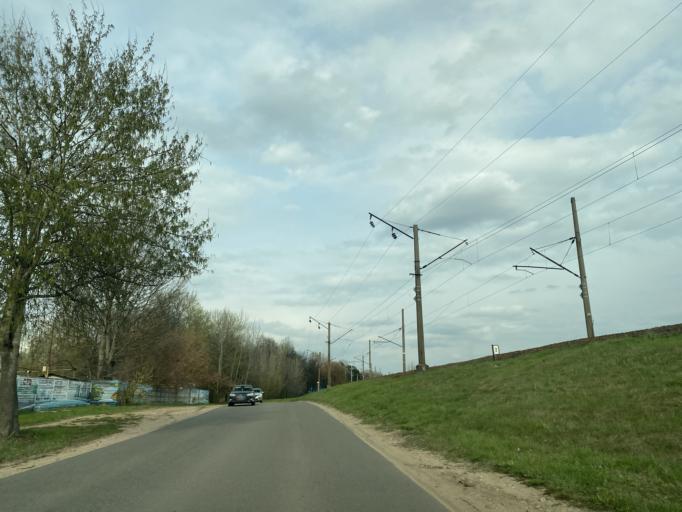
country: BY
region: Minsk
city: Vyaliki Trastsyanets
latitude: 53.9210
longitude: 27.6743
